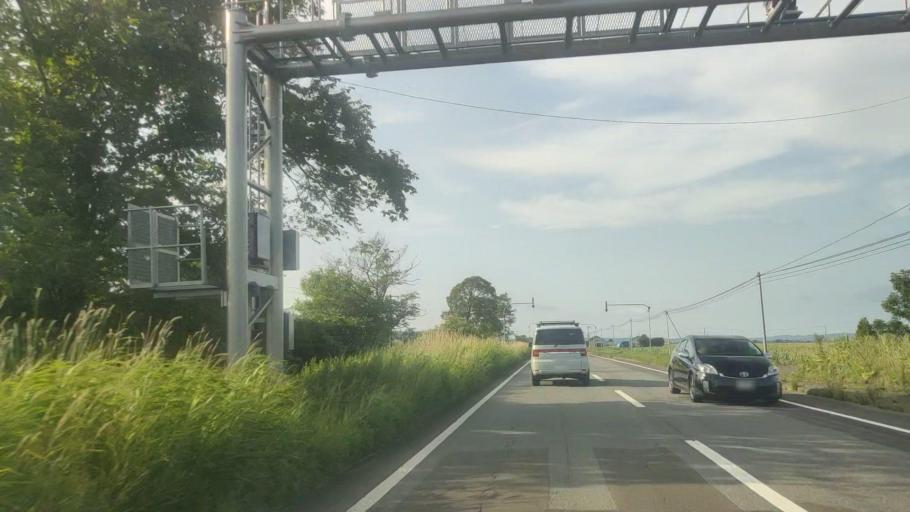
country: JP
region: Hokkaido
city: Chitose
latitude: 42.9594
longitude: 141.7980
